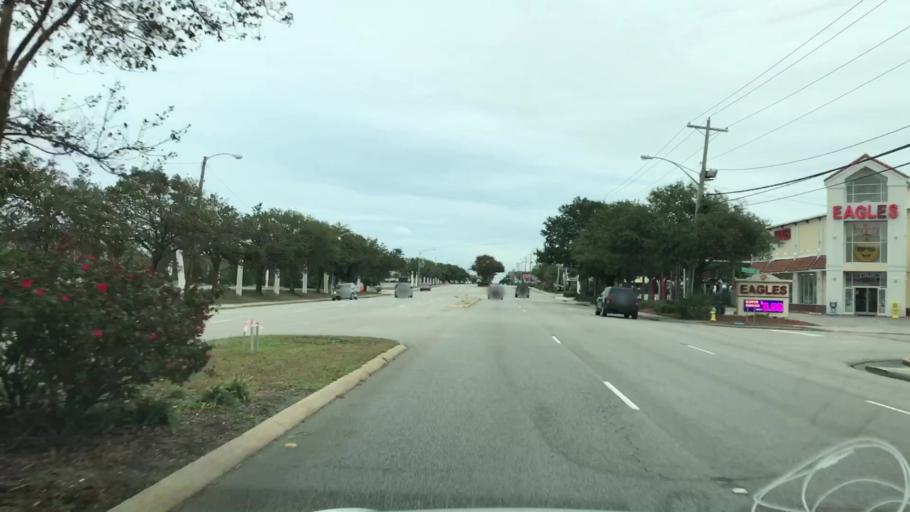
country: US
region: South Carolina
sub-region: Horry County
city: Myrtle Beach
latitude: 33.7048
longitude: -78.8690
